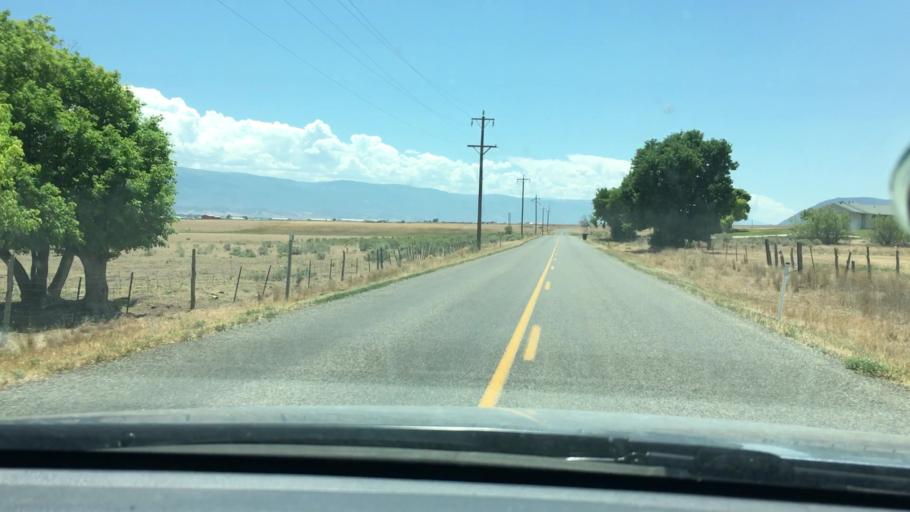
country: US
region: Utah
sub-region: Sanpete County
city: Fountain Green
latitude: 39.5869
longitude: -111.6417
